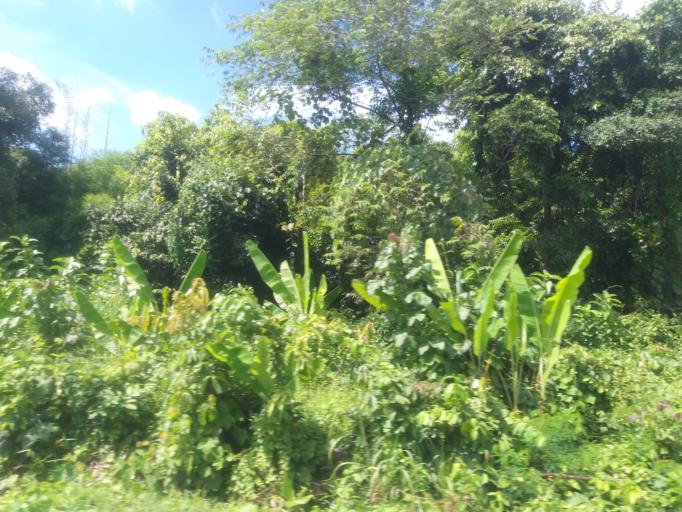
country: TH
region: Nakhon Nayok
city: Nakhon Nayok
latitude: 14.2736
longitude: 101.2906
